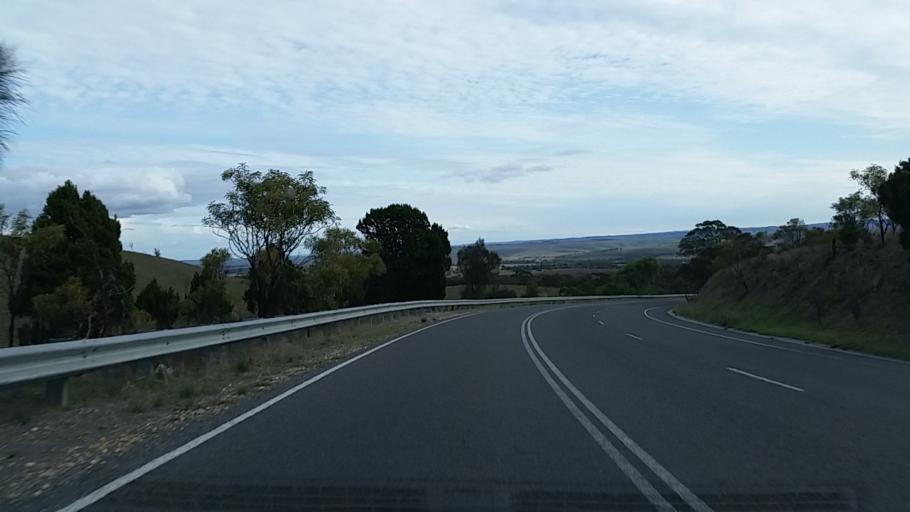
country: AU
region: South Australia
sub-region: Mount Barker
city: Callington
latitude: -35.1140
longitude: 139.0701
